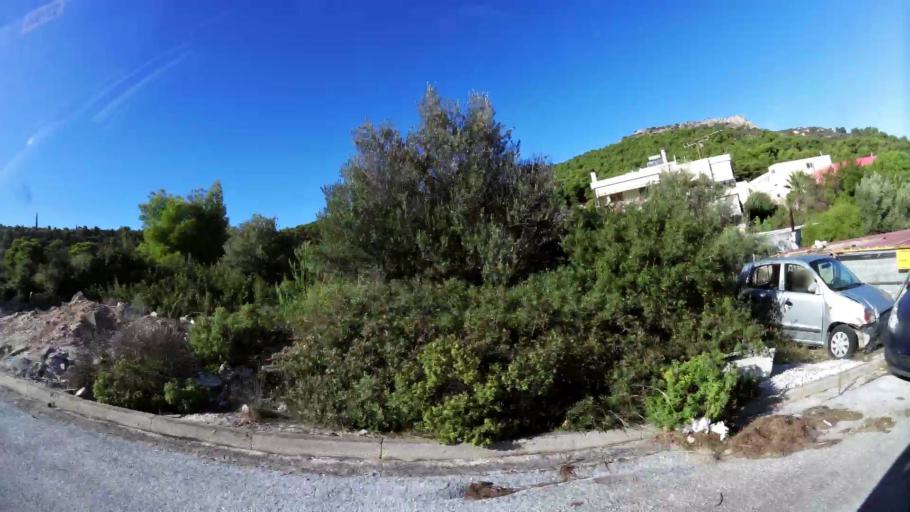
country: GR
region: Attica
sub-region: Nomarchia Anatolikis Attikis
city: Leondarion
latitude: 37.9988
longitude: 23.8427
